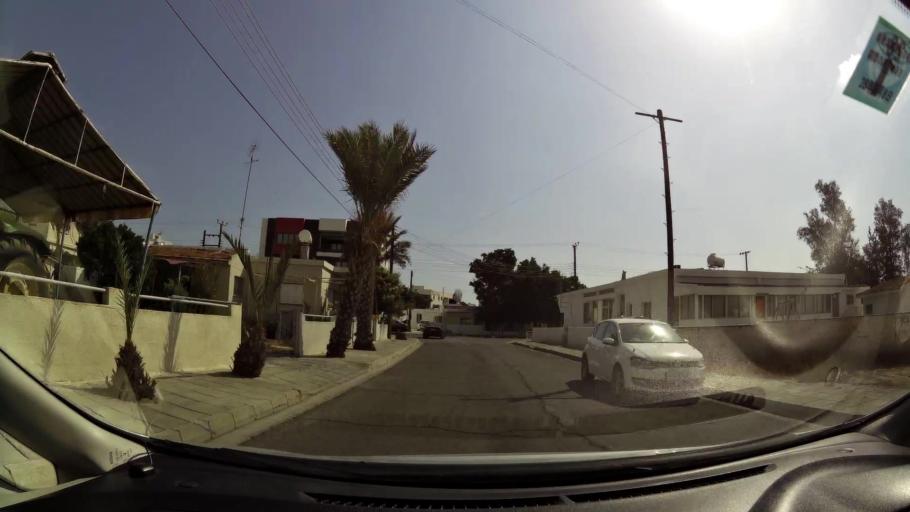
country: CY
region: Larnaka
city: Aradippou
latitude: 34.9384
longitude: 33.5898
